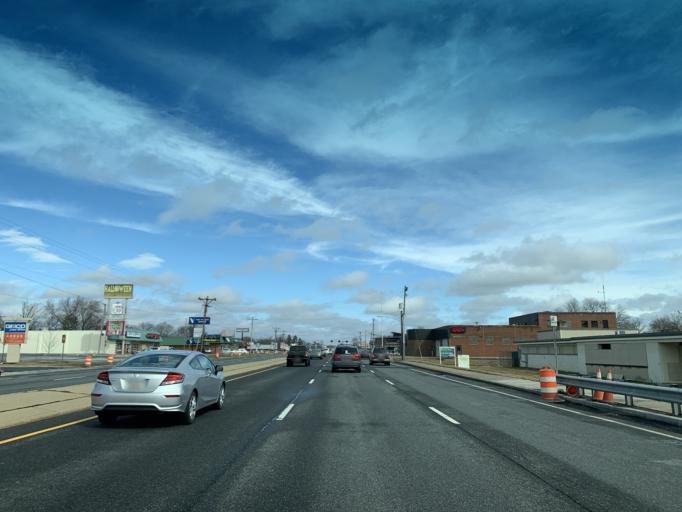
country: US
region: Delaware
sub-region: New Castle County
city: Newport
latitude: 39.7300
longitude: -75.6461
